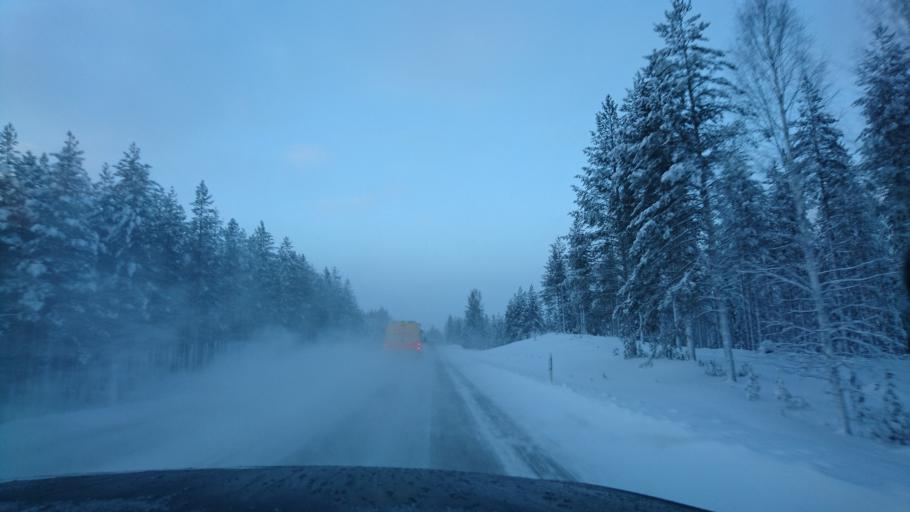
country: FI
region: Northern Ostrobothnia
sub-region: Koillismaa
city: Taivalkoski
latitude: 65.4851
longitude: 27.8245
